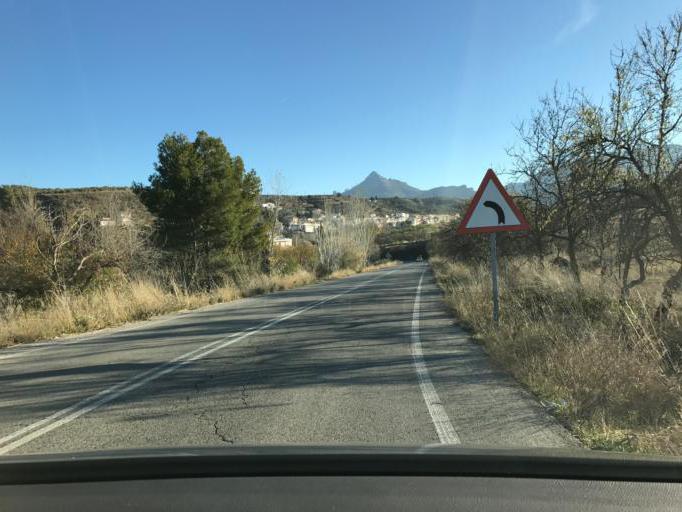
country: ES
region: Andalusia
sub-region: Provincia de Granada
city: Calicasas
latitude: 37.2708
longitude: -3.6285
